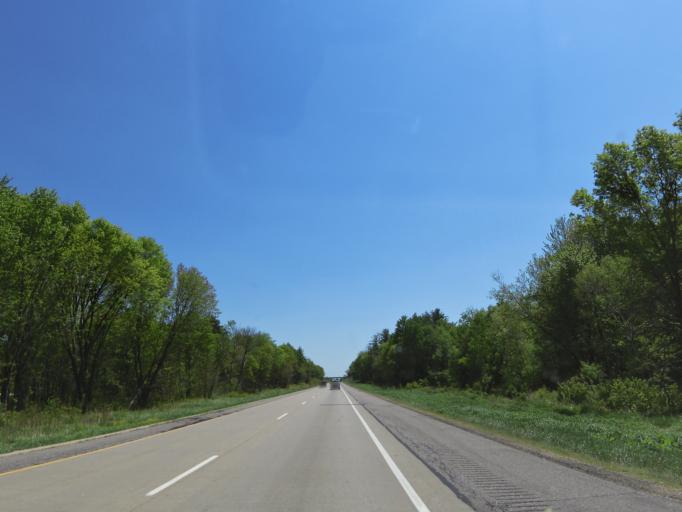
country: US
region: Wisconsin
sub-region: Juneau County
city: New Lisbon
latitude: 43.8675
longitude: -90.1223
